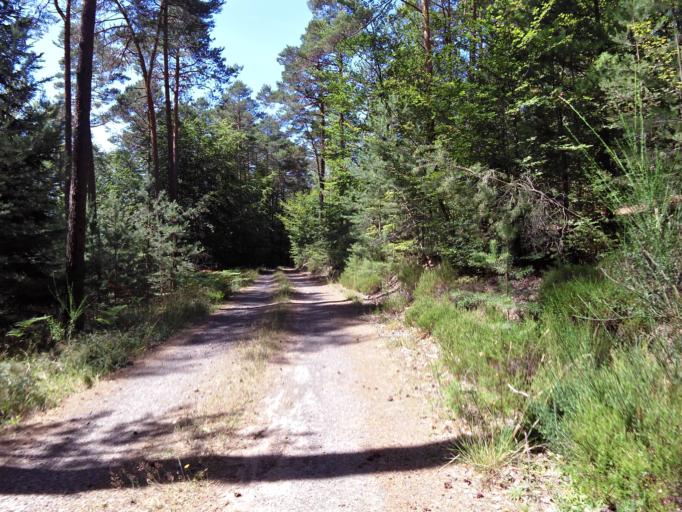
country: DE
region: Rheinland-Pfalz
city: Carlsberg
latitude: 49.4739
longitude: 8.0239
